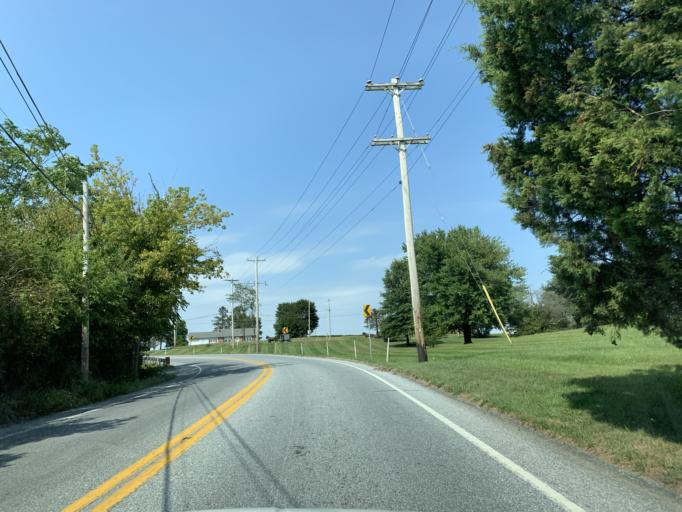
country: US
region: Pennsylvania
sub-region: York County
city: Susquehanna Trails
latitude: 39.7729
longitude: -76.3338
